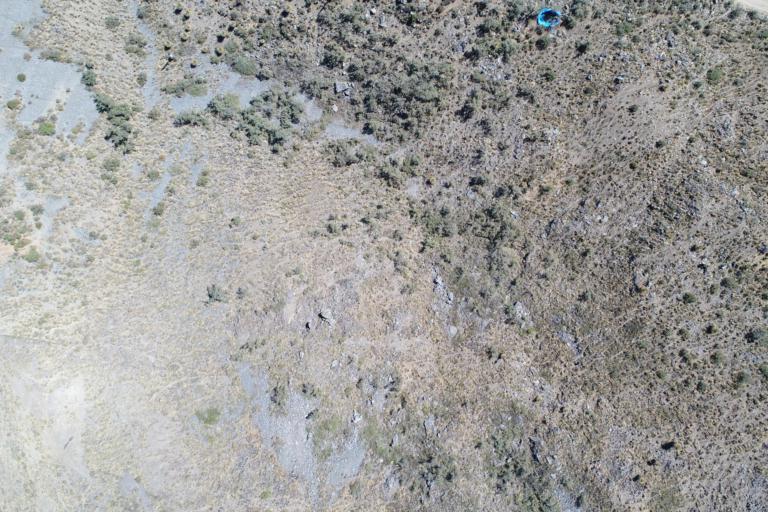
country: BO
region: La Paz
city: Viloco
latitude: -16.8053
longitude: -67.5562
